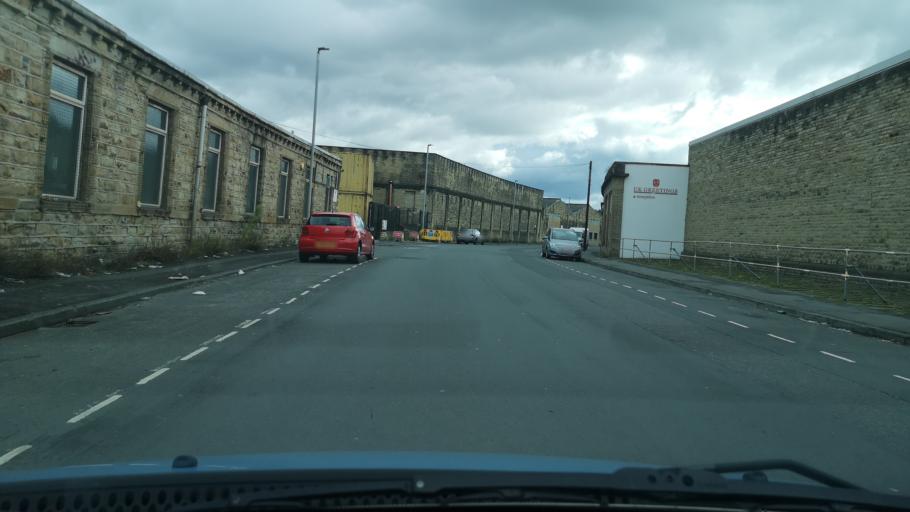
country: GB
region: England
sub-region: Kirklees
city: Dewsbury
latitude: 53.6862
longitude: -1.6249
